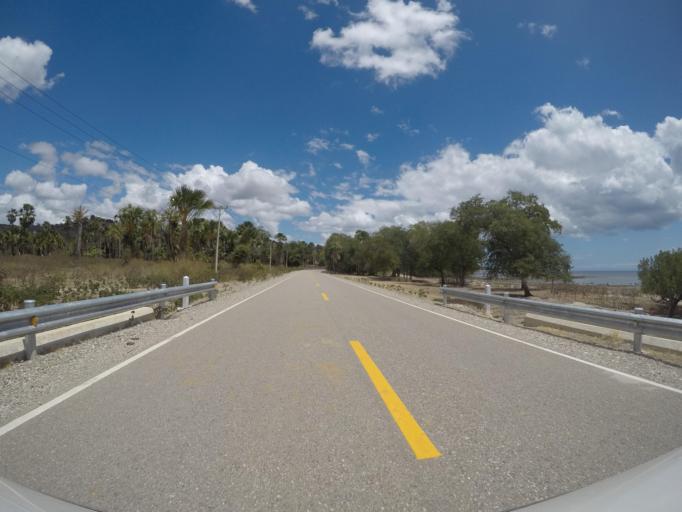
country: TL
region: Lautem
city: Lospalos
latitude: -8.4225
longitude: 126.7679
